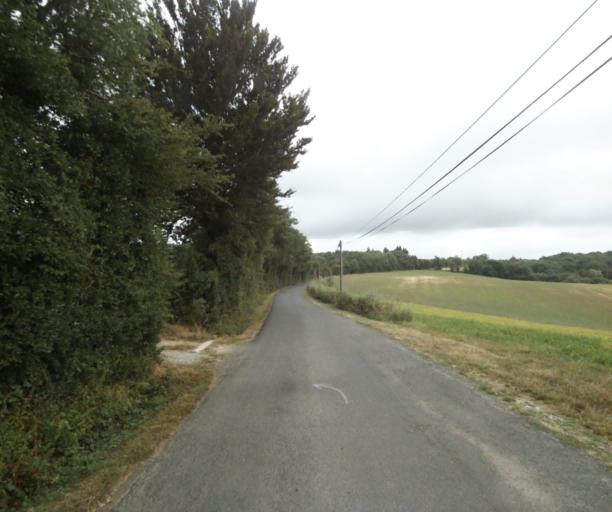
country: FR
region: Midi-Pyrenees
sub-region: Departement du Tarn
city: Soreze
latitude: 43.3982
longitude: 2.0576
